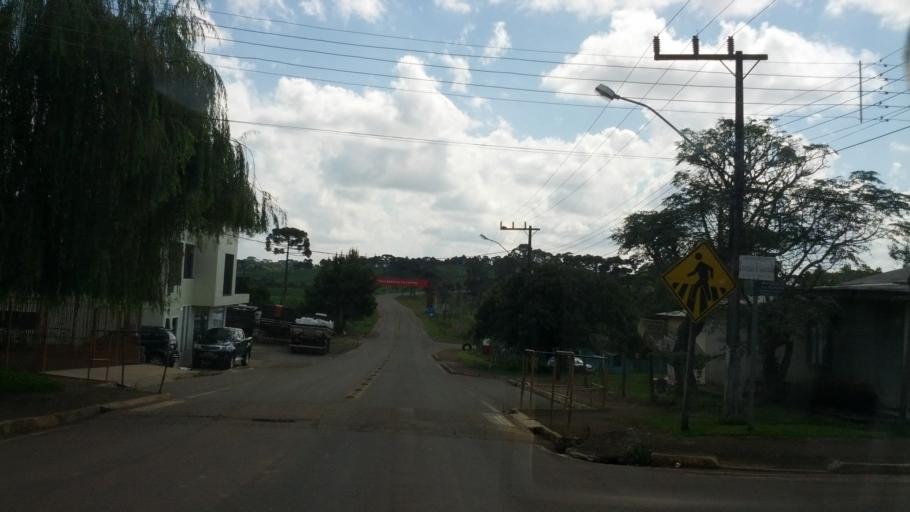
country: BR
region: Rio Grande do Sul
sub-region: Vacaria
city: Estrela
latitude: -27.7977
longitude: -50.8763
